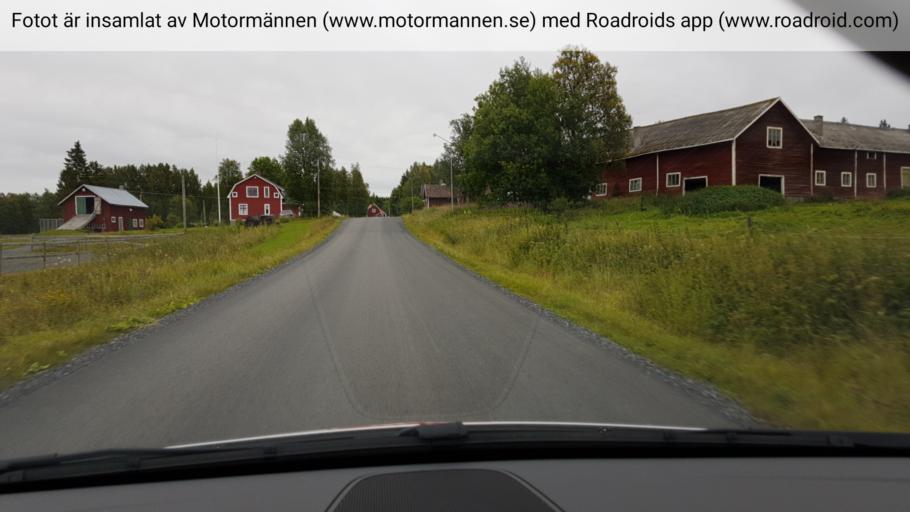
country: SE
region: Jaemtland
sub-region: OEstersunds Kommun
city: Lit
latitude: 63.5624
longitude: 14.9427
